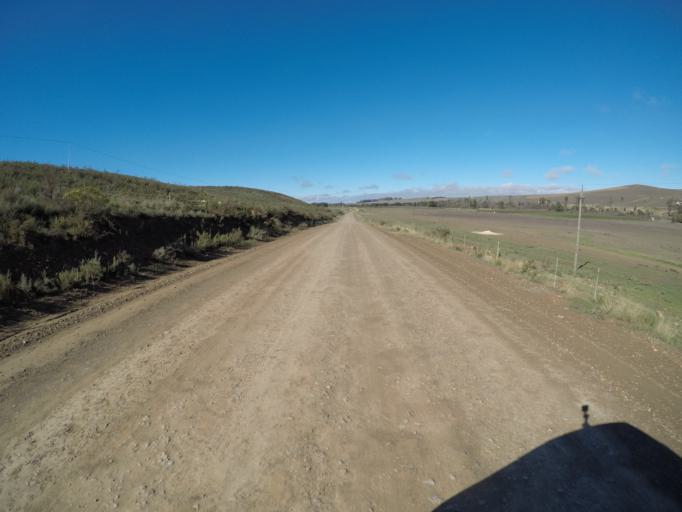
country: ZA
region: Western Cape
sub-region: Overberg District Municipality
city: Caledon
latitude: -34.0901
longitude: 19.6607
